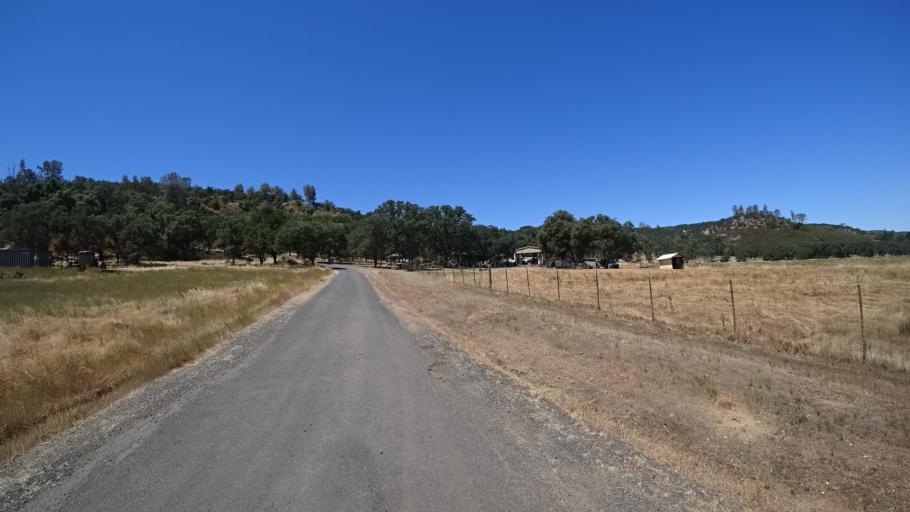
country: US
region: California
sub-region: Calaveras County
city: Copperopolis
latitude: 37.9603
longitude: -120.6997
